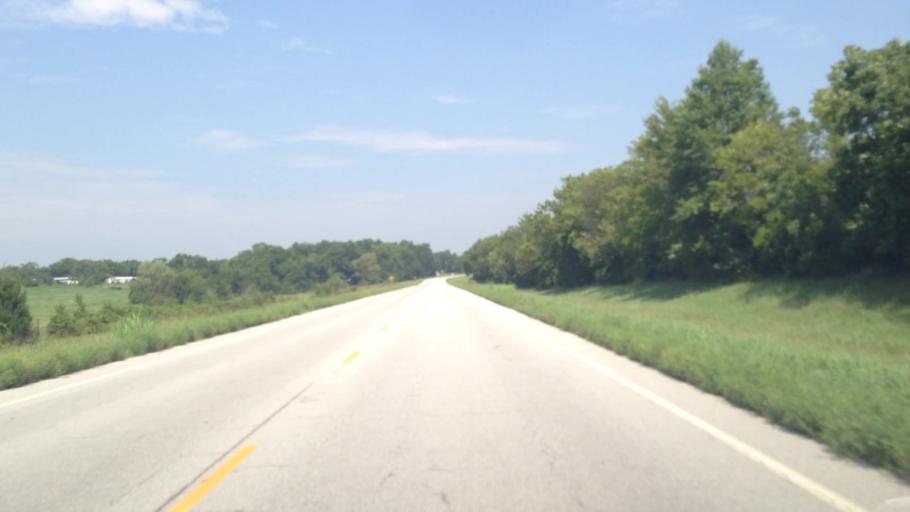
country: US
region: Kansas
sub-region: Labette County
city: Oswego
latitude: 37.1502
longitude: -95.1054
